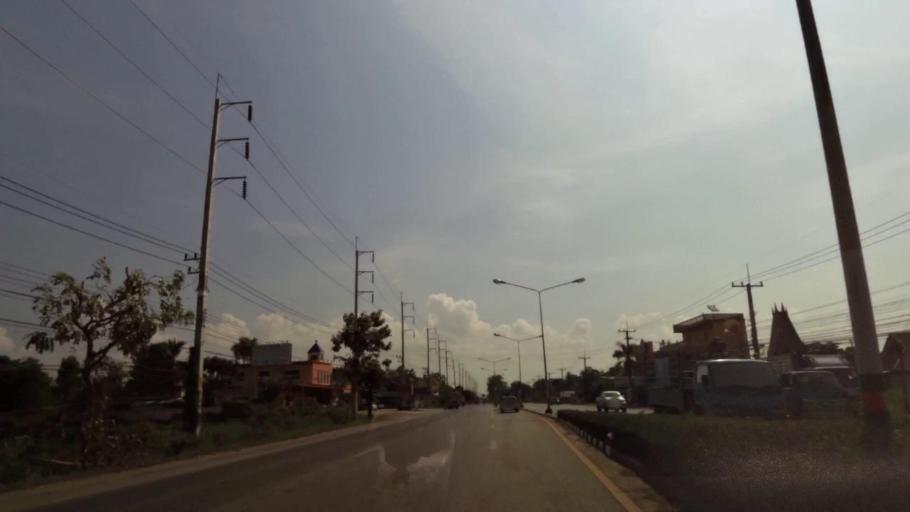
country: TH
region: Uttaradit
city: Uttaradit
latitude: 17.5924
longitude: 100.1318
